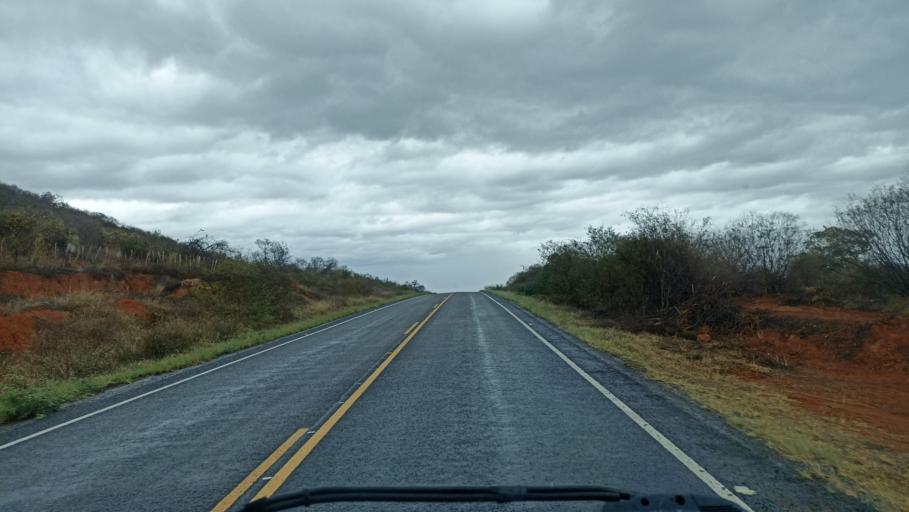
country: BR
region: Bahia
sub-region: Iacu
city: Iacu
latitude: -12.9596
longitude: -40.4757
